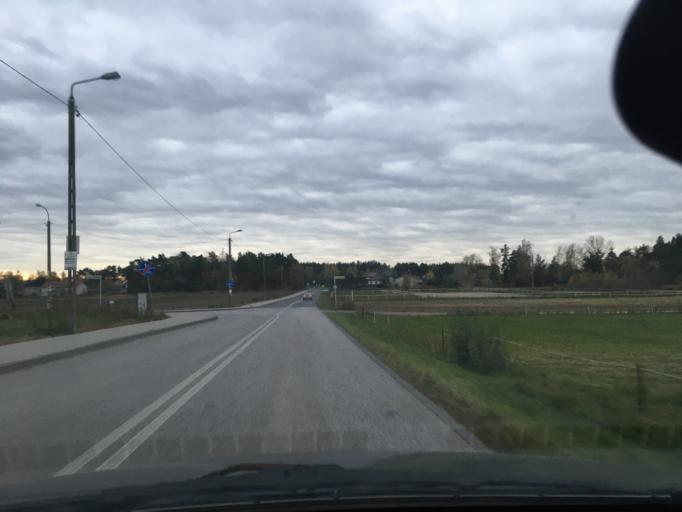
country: PL
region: Masovian Voivodeship
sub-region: Powiat piaseczynski
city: Lesznowola
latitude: 52.0705
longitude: 20.9349
